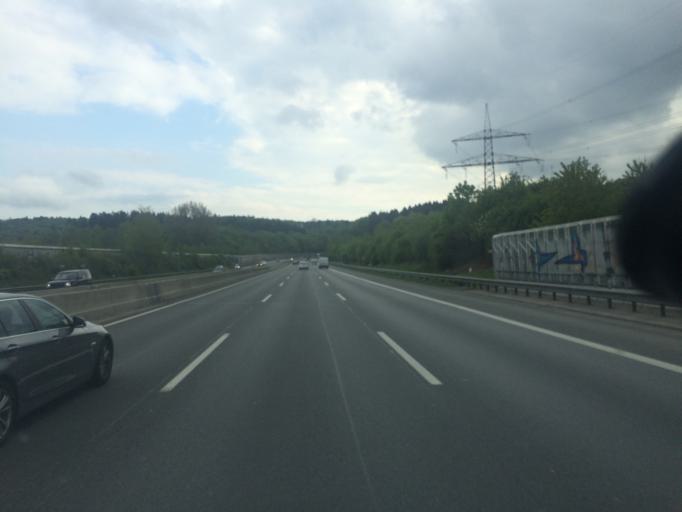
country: DE
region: North Rhine-Westphalia
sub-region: Regierungsbezirk Detmold
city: Oerlinghausen
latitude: 51.9792
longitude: 8.6155
